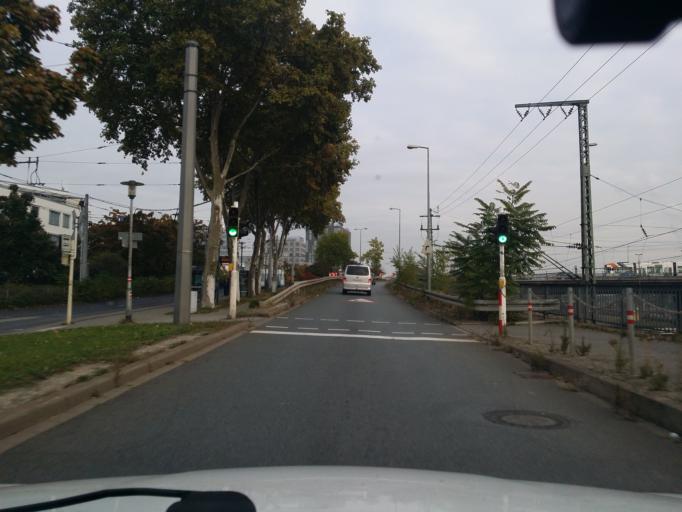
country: DE
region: Rheinland-Pfalz
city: Ludwigshafen am Rhein
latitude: 49.4818
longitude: 8.4647
